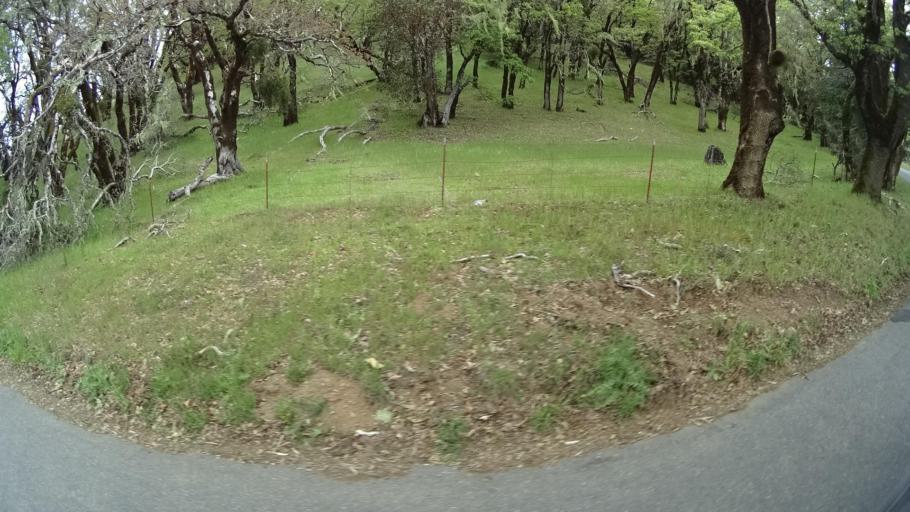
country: US
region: California
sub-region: Humboldt County
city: Redway
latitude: 40.1543
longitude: -123.5574
